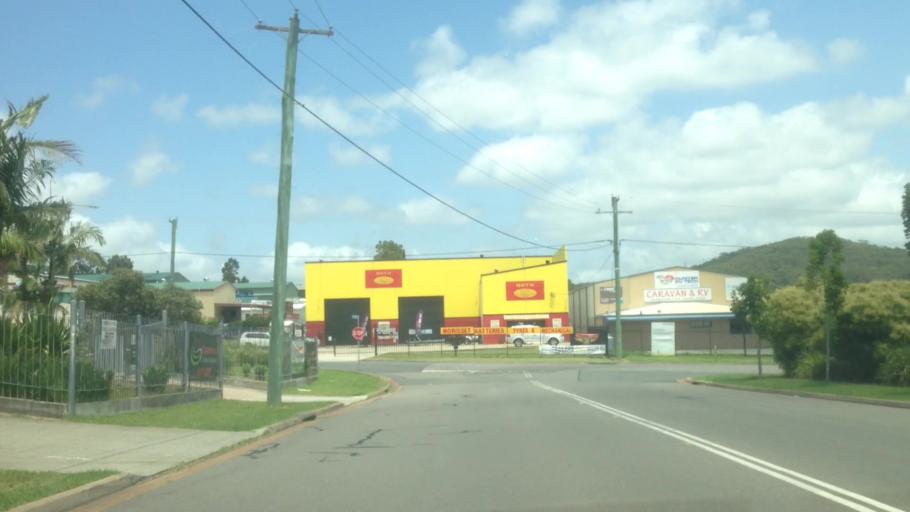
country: AU
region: New South Wales
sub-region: Lake Macquarie Shire
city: Dora Creek
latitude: -33.1170
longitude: 151.4725
